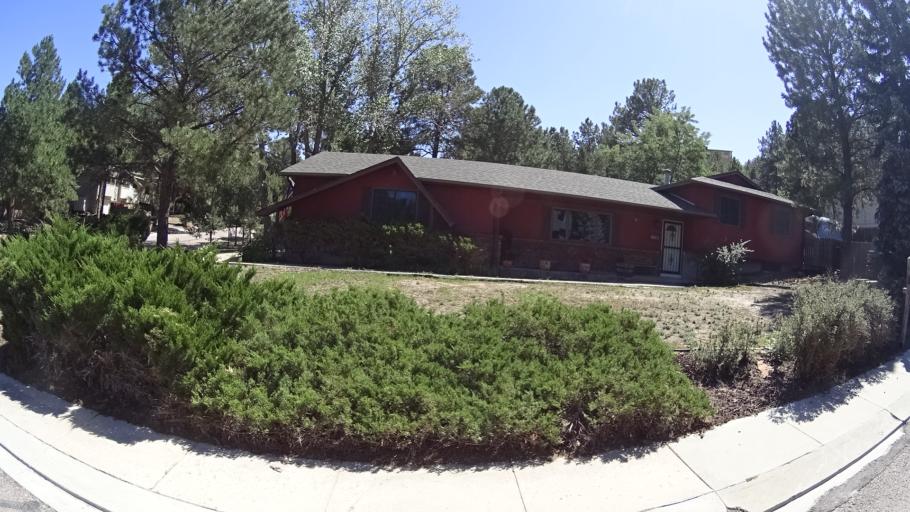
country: US
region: Colorado
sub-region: El Paso County
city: Colorado Springs
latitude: 38.9225
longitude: -104.8049
